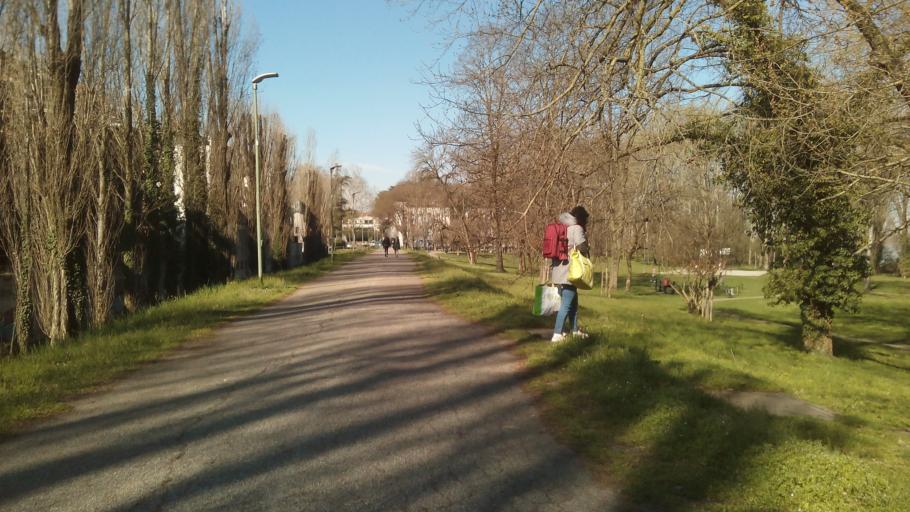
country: IT
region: Lombardy
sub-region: Provincia di Mantova
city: Mantova
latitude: 45.1565
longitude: 10.7740
